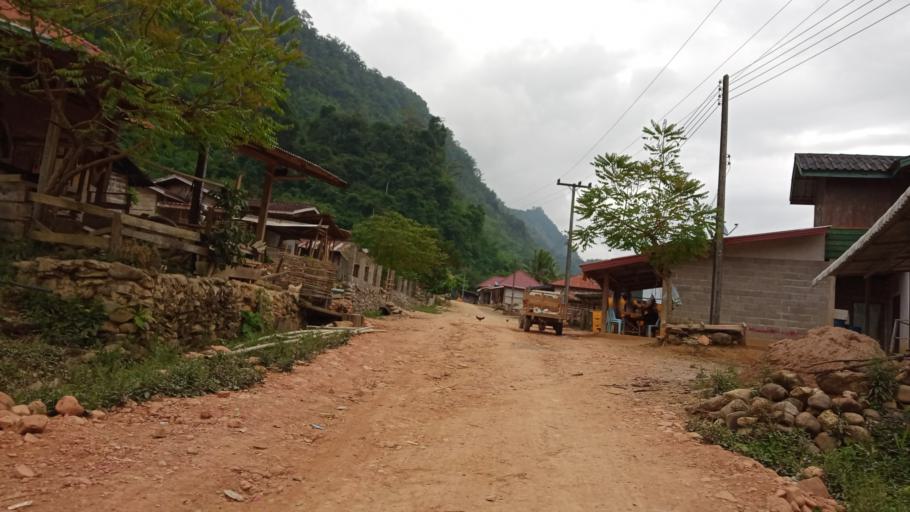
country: LA
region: Xiangkhoang
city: Phonsavan
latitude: 19.0926
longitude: 103.0022
